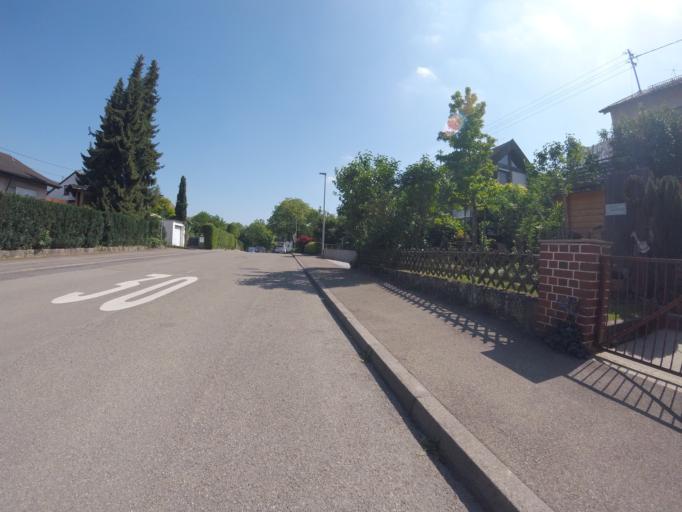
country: DE
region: Baden-Wuerttemberg
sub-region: Regierungsbezirk Stuttgart
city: Steinheim am der Murr
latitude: 48.9773
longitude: 9.2904
